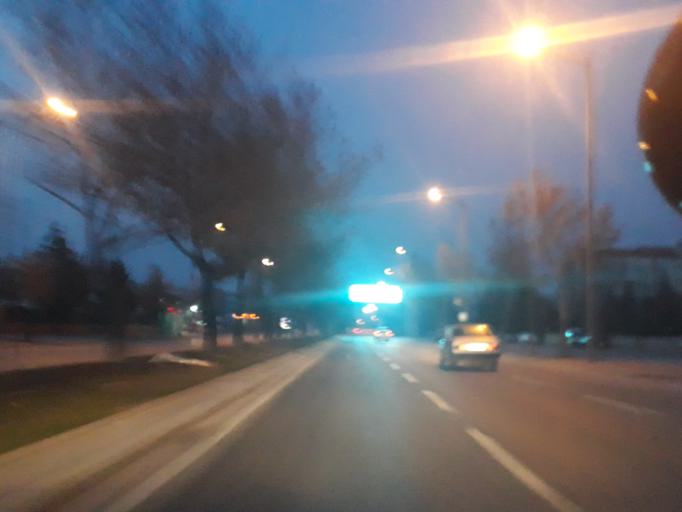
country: TR
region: Konya
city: Selcuklu
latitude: 37.9016
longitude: 32.5099
